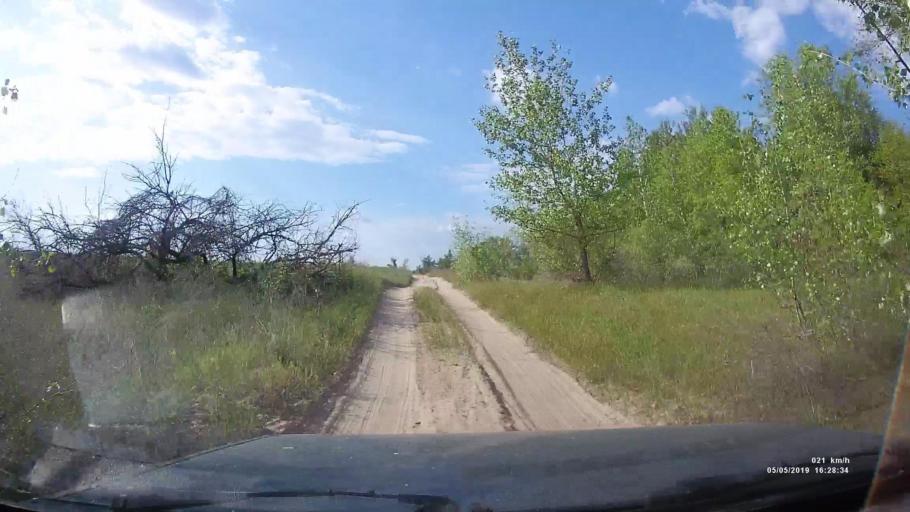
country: RU
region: Rostov
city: Ust'-Donetskiy
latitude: 47.7679
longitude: 41.0159
